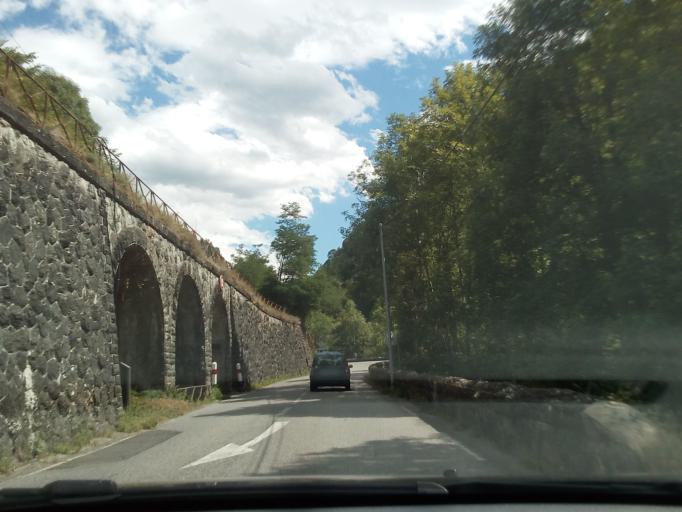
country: FR
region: Aquitaine
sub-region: Departement des Pyrenees-Atlantiques
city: Laruns
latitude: 42.9337
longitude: -0.5863
